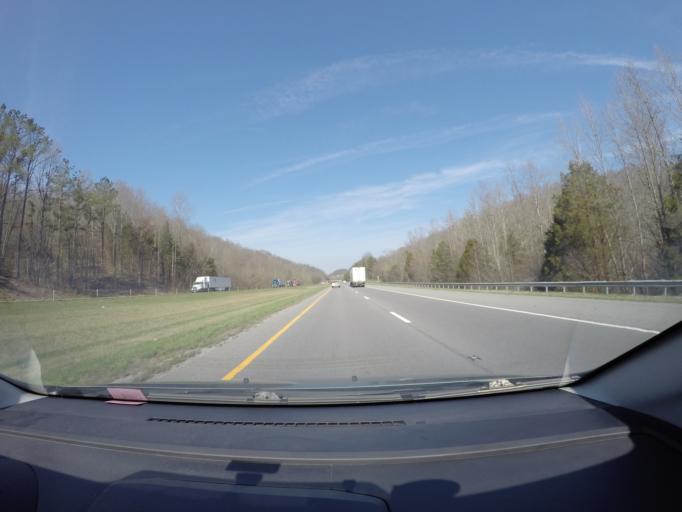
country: US
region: Tennessee
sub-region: Coffee County
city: New Union
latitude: 35.5530
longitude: -86.1952
